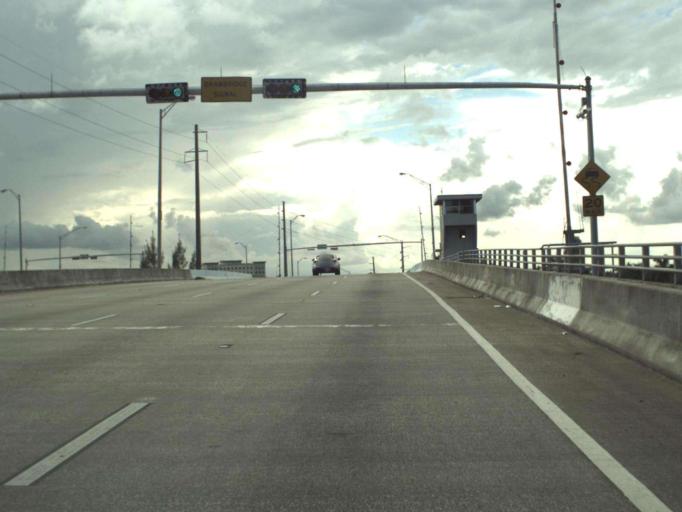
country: US
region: Florida
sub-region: Miami-Dade County
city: Sunny Isles Beach
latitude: 25.9304
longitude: -80.1295
